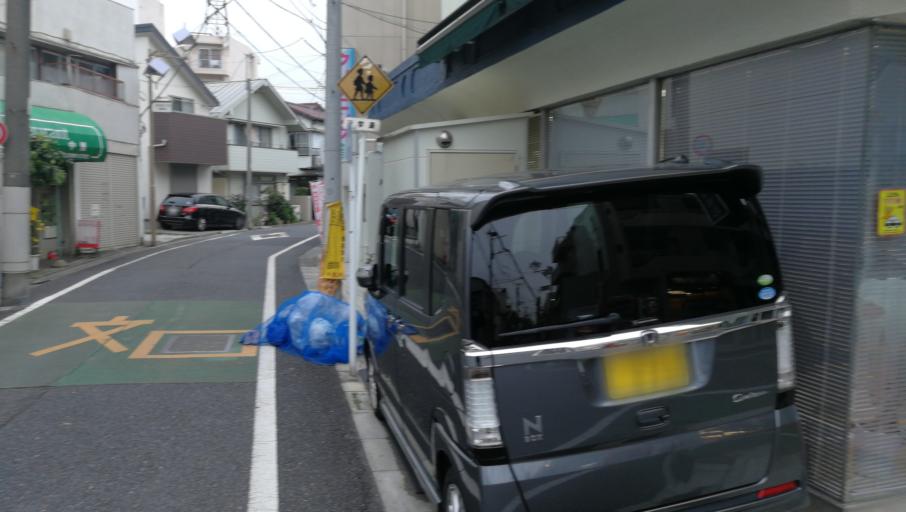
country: JP
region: Tokyo
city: Tokyo
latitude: 35.7259
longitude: 139.6684
